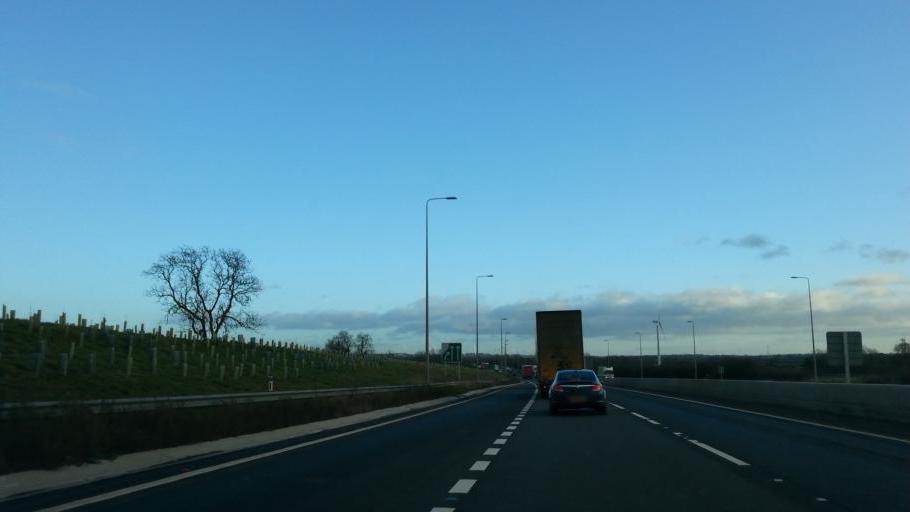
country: GB
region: England
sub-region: Leicestershire
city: Lutterworth
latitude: 52.4024
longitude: -1.1693
